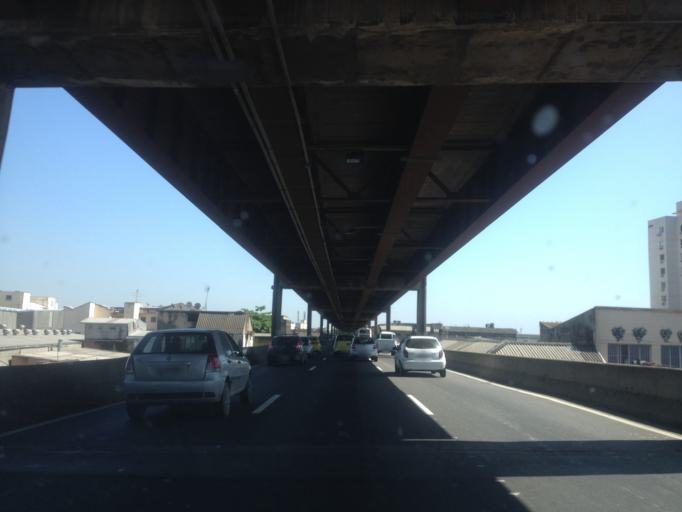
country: BR
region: Rio de Janeiro
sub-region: Rio De Janeiro
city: Rio de Janeiro
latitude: -22.8940
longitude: -43.2203
